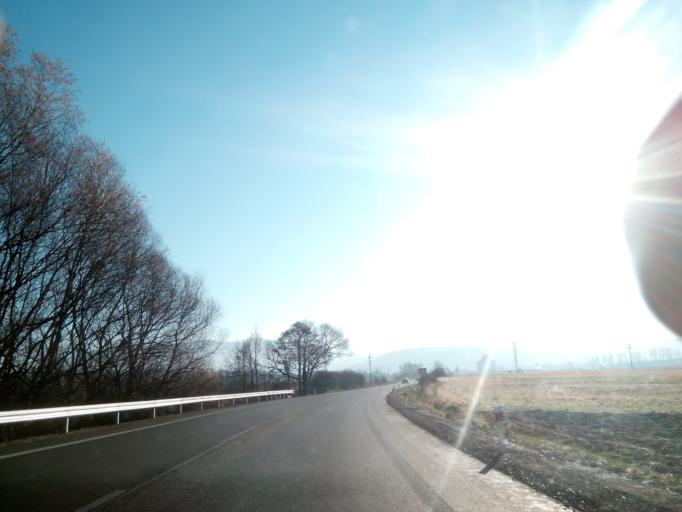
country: SK
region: Kosicky
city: Kosice
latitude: 48.7357
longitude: 21.4315
